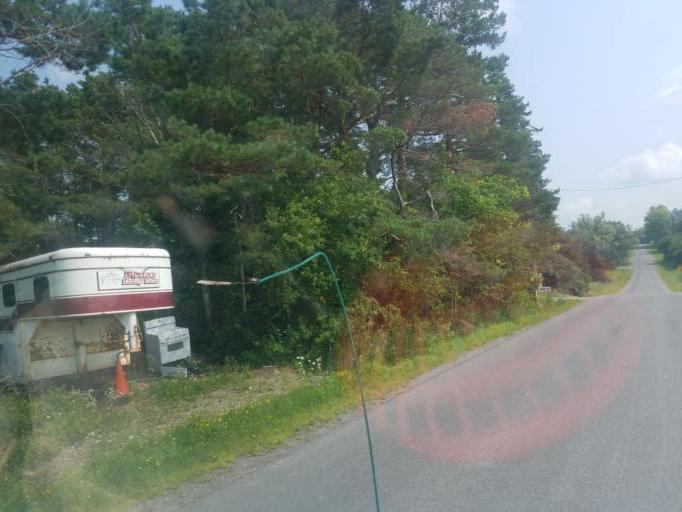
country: US
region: New York
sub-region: Montgomery County
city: Wellsville
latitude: 42.8510
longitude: -74.3482
